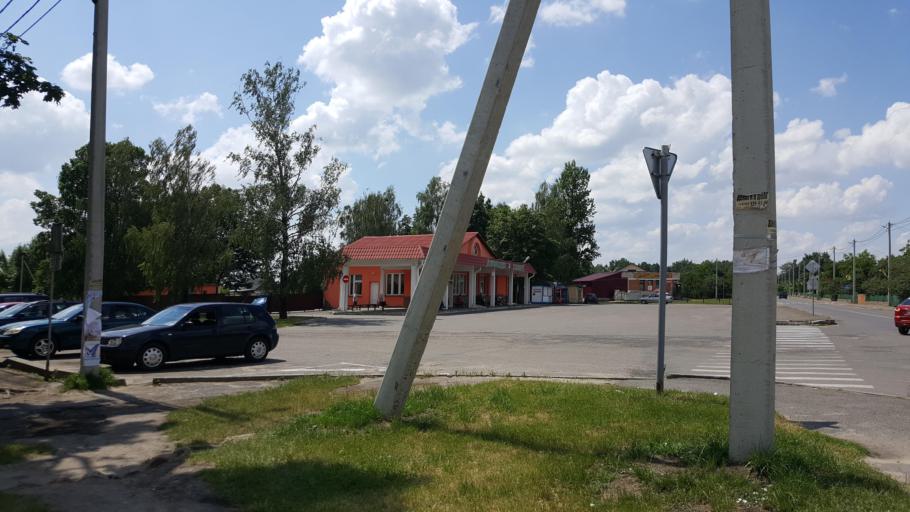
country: BY
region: Brest
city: Kamyanyets
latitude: 52.4038
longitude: 23.8130
